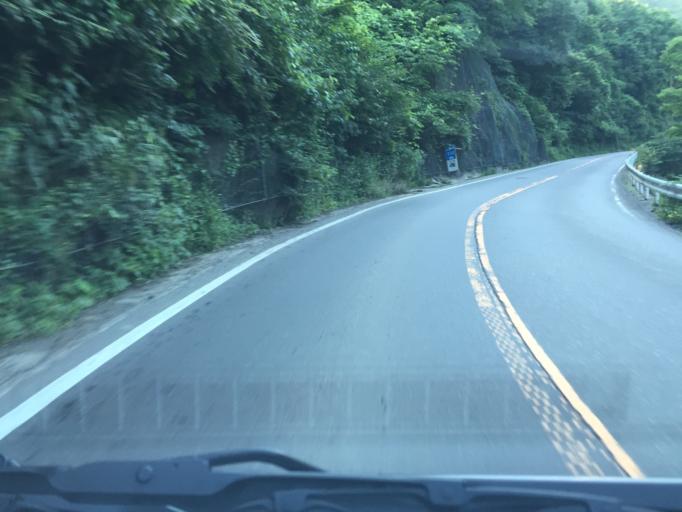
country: JP
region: Fukushima
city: Yanagawamachi-saiwaicho
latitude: 37.7561
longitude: 140.6668
